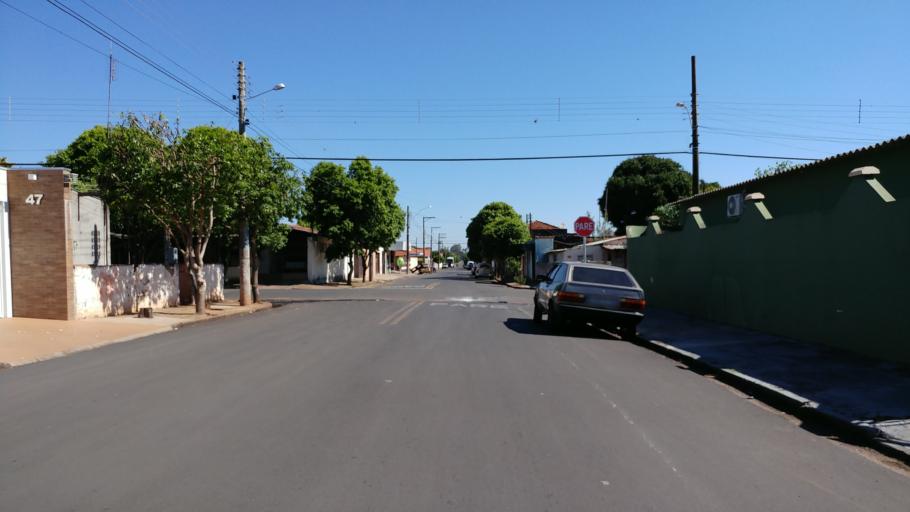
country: BR
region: Sao Paulo
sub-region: Paraguacu Paulista
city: Paraguacu Paulista
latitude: -22.4222
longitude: -50.5831
